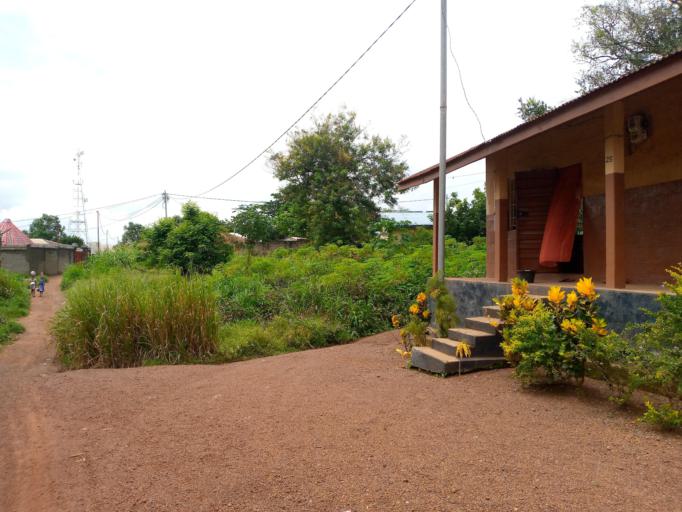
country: SL
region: Northern Province
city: Magburaka
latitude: 8.7215
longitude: -11.9377
